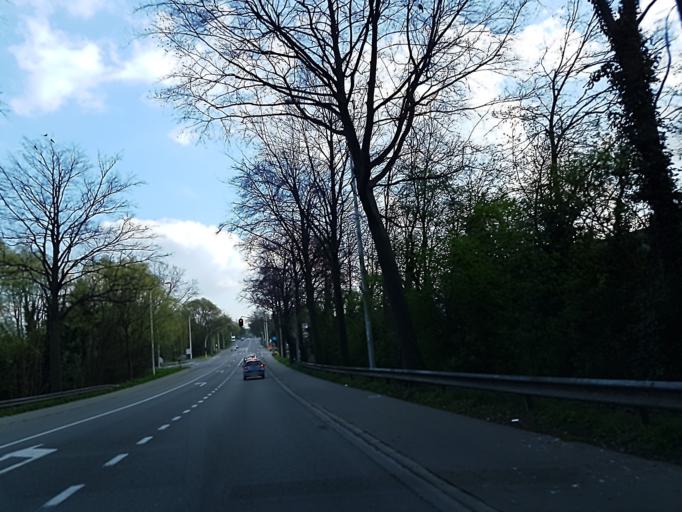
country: BE
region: Flanders
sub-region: Provincie Oost-Vlaanderen
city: Ninove
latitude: 50.8332
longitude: 4.0116
